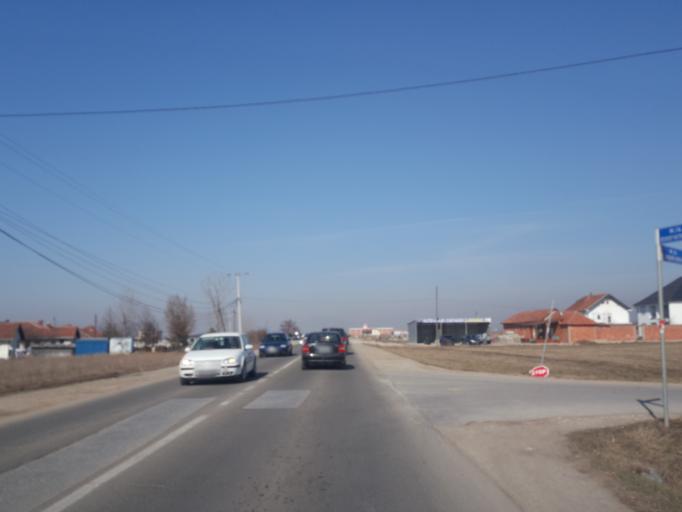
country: XK
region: Mitrovica
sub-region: Vushtrri
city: Vushtrri
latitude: 42.7860
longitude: 21.0087
